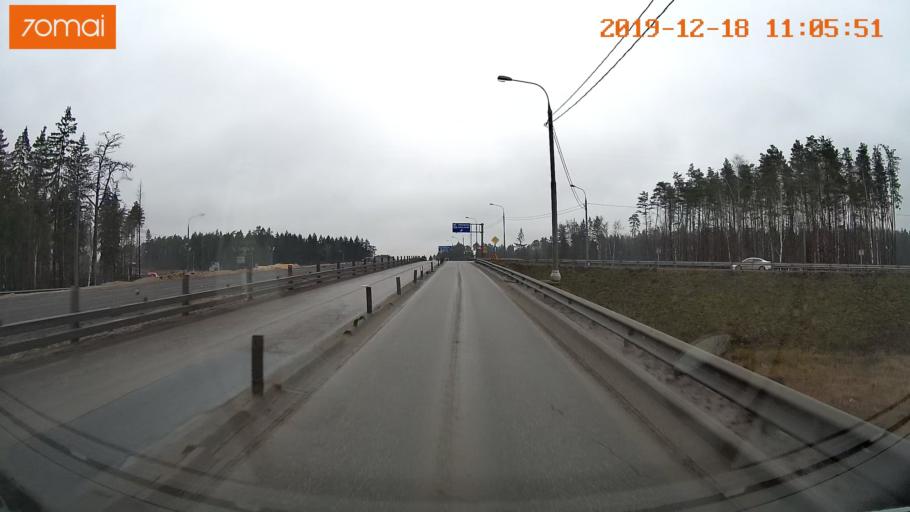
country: RU
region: Moskovskaya
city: Golitsyno
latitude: 55.6019
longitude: 37.0061
